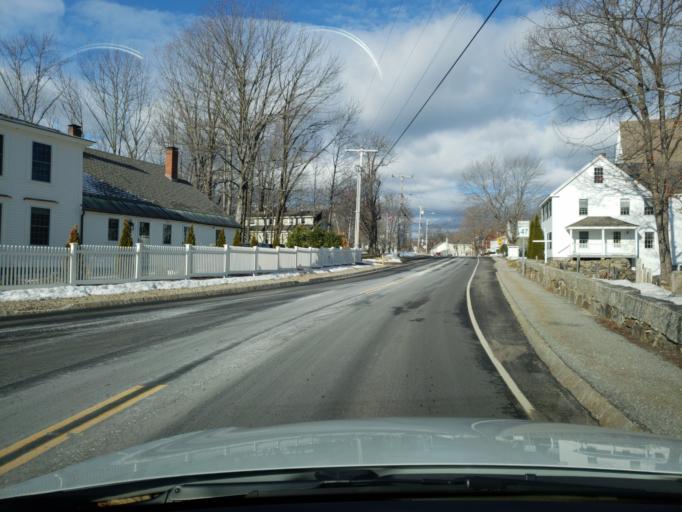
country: US
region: New Hampshire
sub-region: Hillsborough County
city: Greenfield
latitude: 42.9875
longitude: -71.8127
